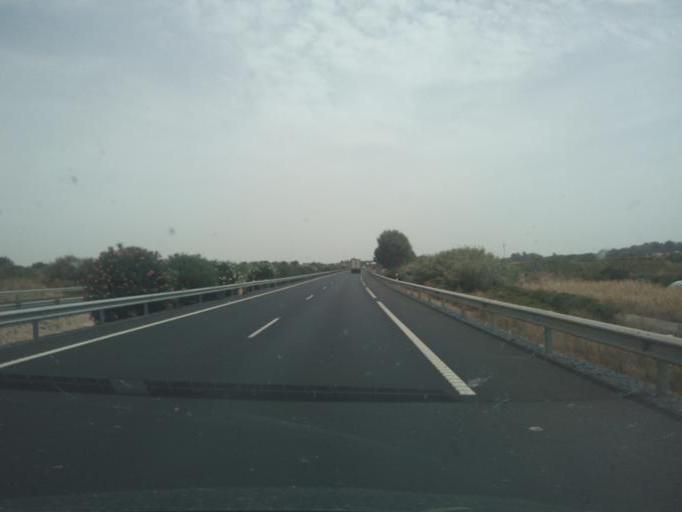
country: ES
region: Andalusia
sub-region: Provincia de Huelva
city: Bollullos par del Condado
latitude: 37.3594
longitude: -6.5233
